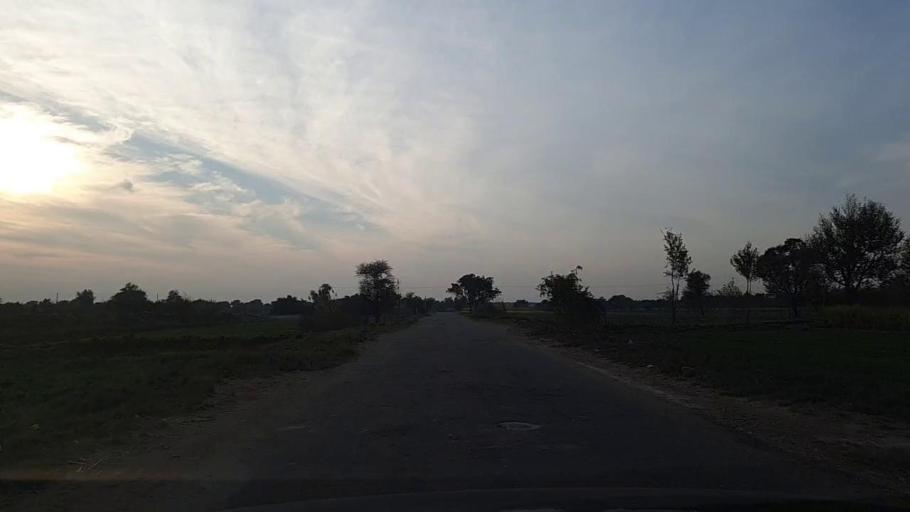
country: PK
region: Sindh
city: Nawabshah
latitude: 26.4031
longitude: 68.4870
